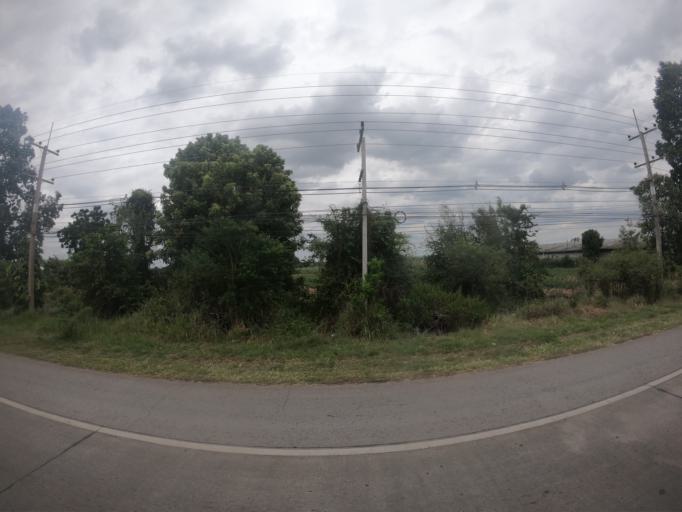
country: TH
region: Nakhon Ratchasima
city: Chok Chai
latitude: 14.7921
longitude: 102.1682
